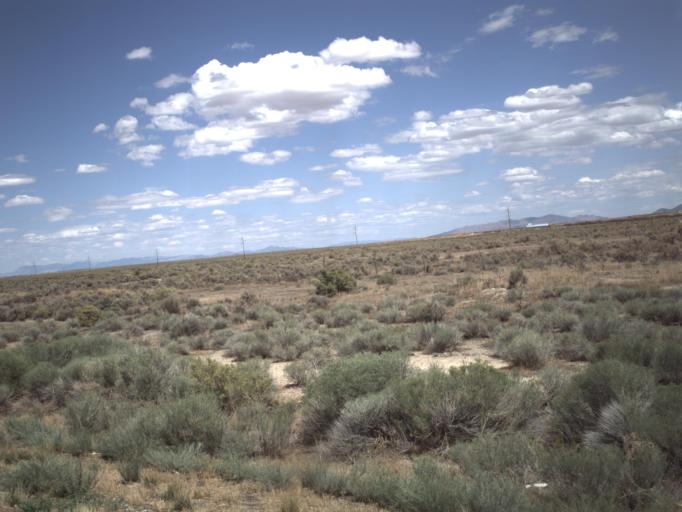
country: US
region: Utah
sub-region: Millard County
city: Delta
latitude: 39.2643
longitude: -112.4497
